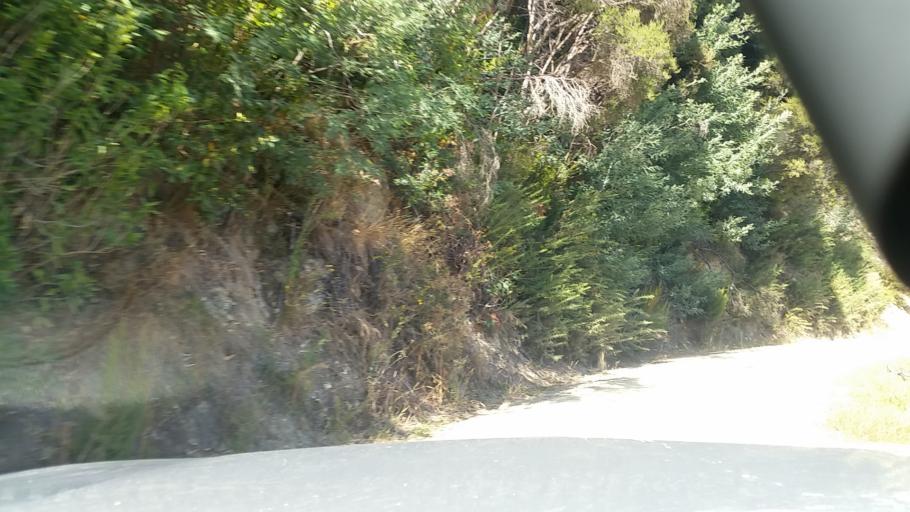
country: NZ
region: Marlborough
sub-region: Marlborough District
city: Picton
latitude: -41.3060
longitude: 174.1754
